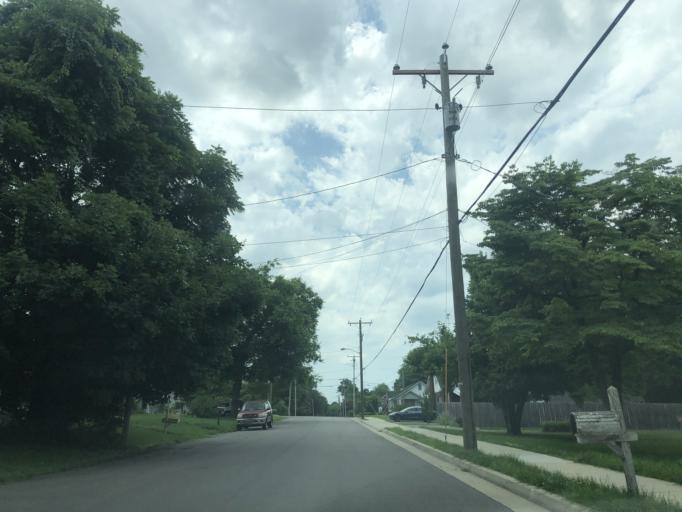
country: US
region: Tennessee
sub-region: Davidson County
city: Nashville
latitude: 36.1845
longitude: -86.7401
